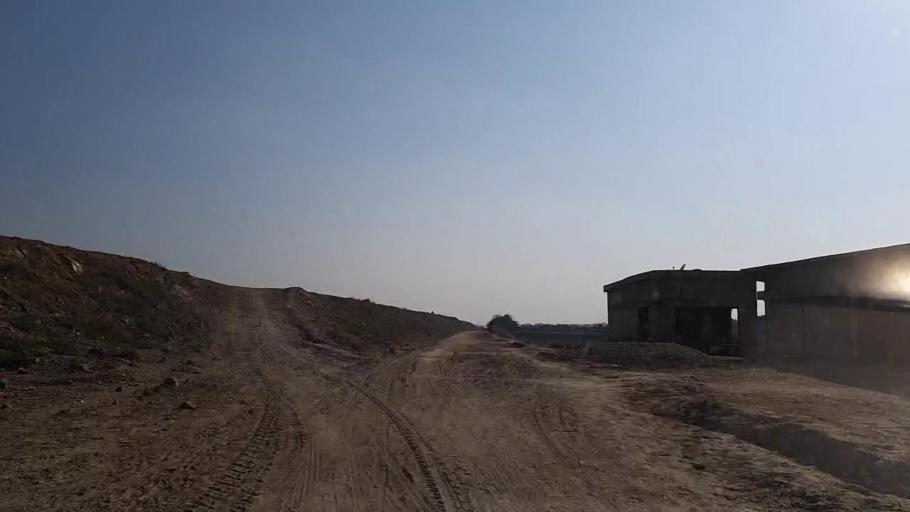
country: PK
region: Sindh
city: Thatta
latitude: 24.7364
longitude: 67.9699
